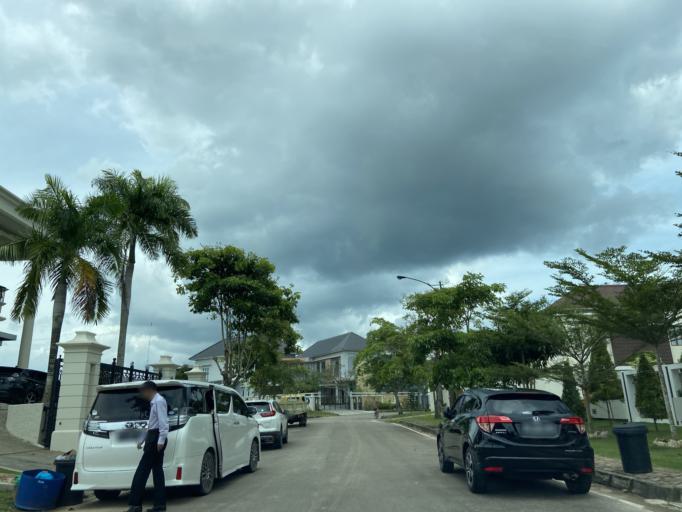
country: SG
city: Singapore
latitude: 1.1273
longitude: 104.0014
